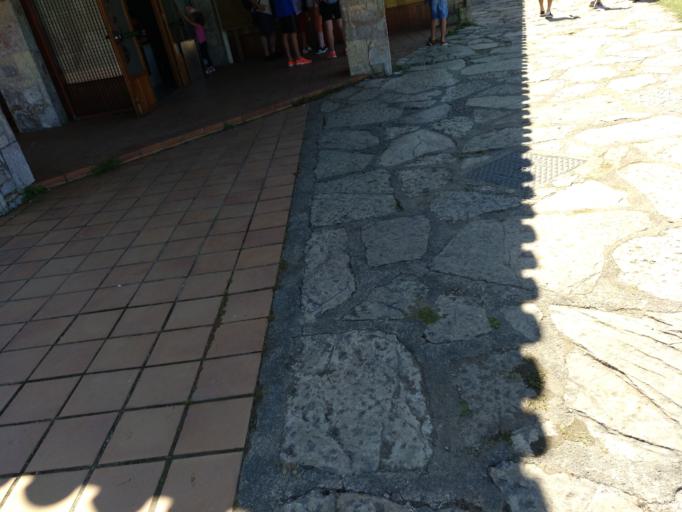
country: ES
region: Asturias
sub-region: Province of Asturias
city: Amieva
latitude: 43.2771
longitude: -4.9833
